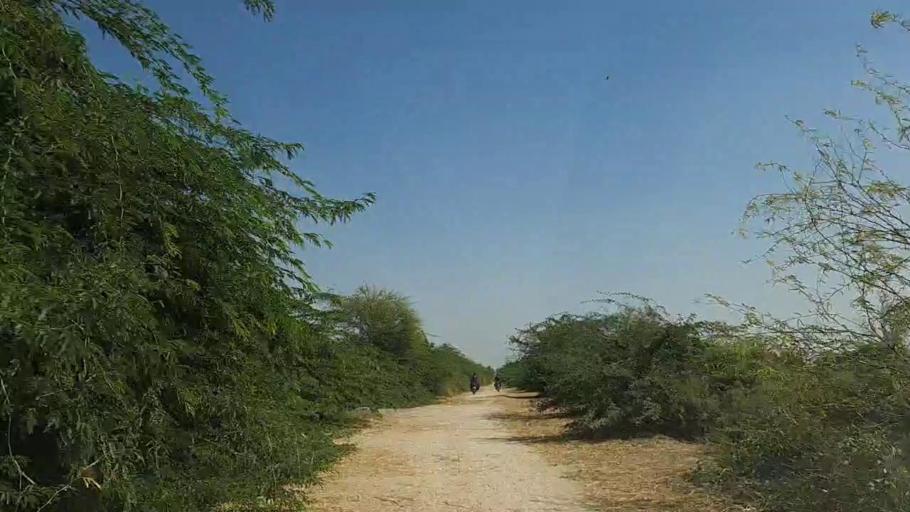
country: PK
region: Sindh
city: Mirpur Batoro
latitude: 24.7313
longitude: 68.2177
